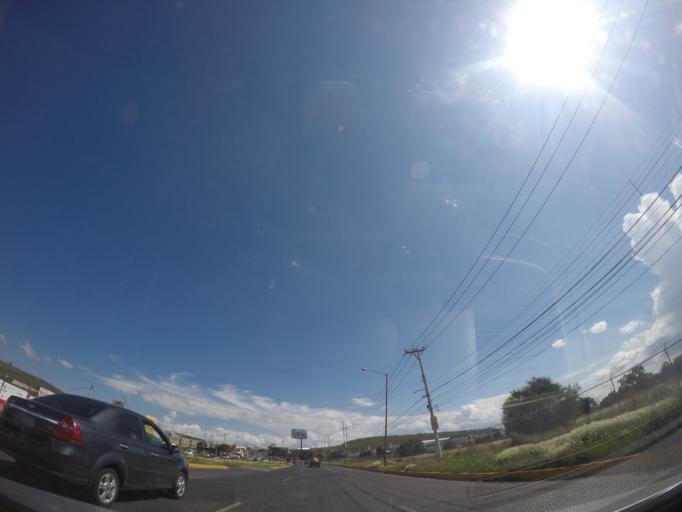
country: MX
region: Hidalgo
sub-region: Mineral de la Reforma
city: Carboneras
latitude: 20.0912
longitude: -98.7144
